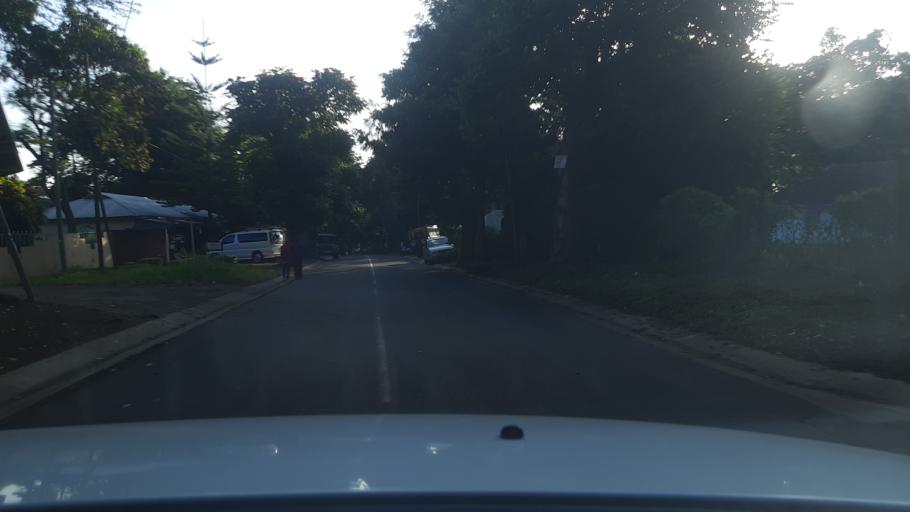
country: TZ
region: Arusha
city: Arusha
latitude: -3.3788
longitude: 36.6999
